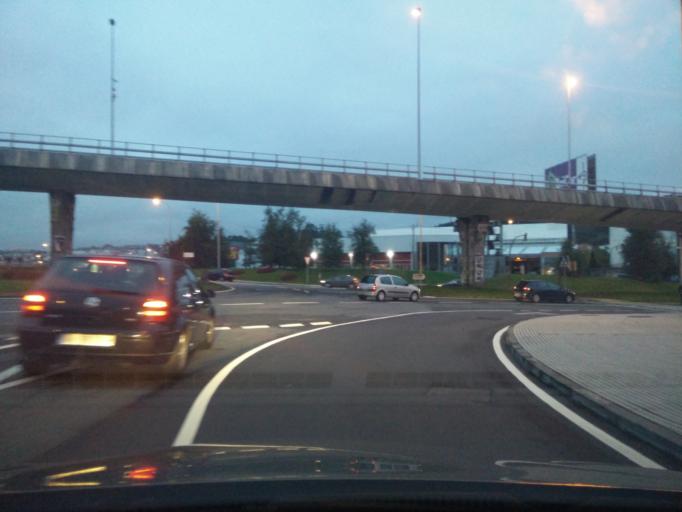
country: ES
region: Galicia
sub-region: Provincia da Coruna
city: A Coruna
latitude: 43.3491
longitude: -8.4209
